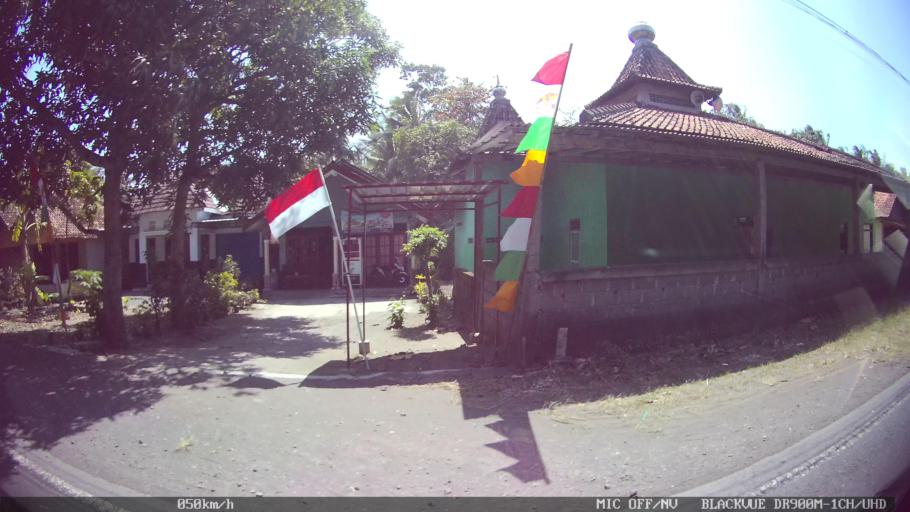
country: ID
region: Daerah Istimewa Yogyakarta
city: Srandakan
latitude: -7.9236
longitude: 110.1191
